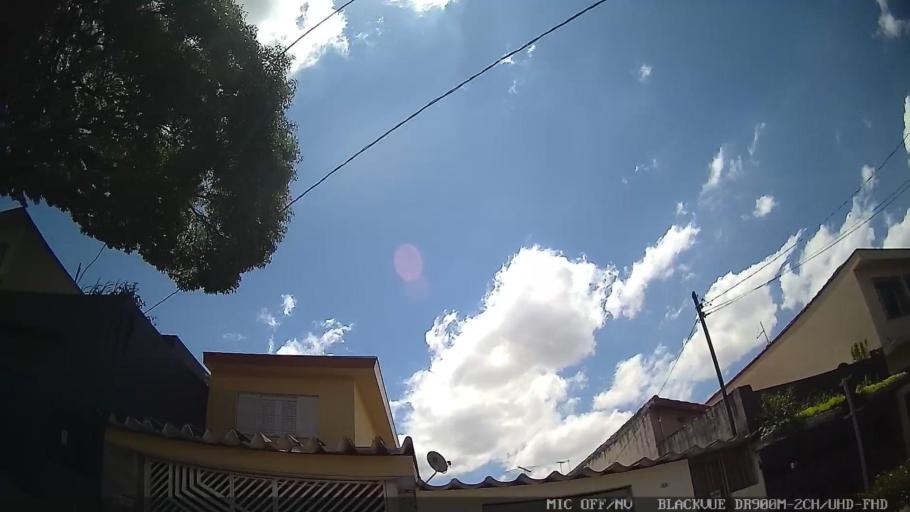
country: BR
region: Sao Paulo
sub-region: Diadema
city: Diadema
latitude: -23.6521
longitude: -46.6550
